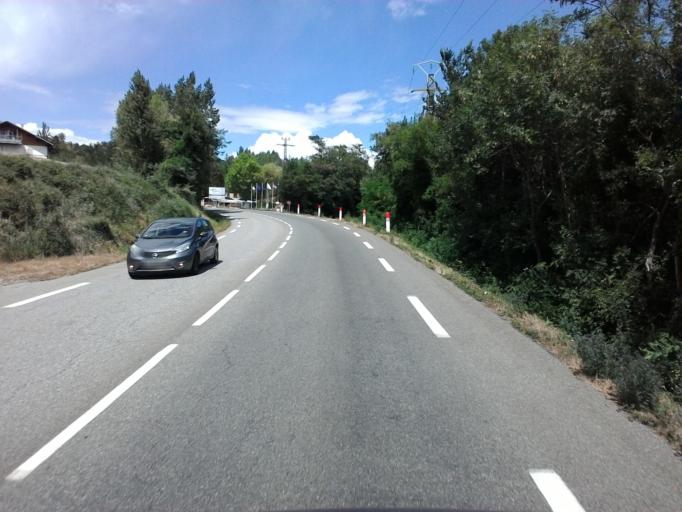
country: FR
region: Provence-Alpes-Cote d'Azur
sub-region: Departement des Hautes-Alpes
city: Gap
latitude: 44.5789
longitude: 6.0818
